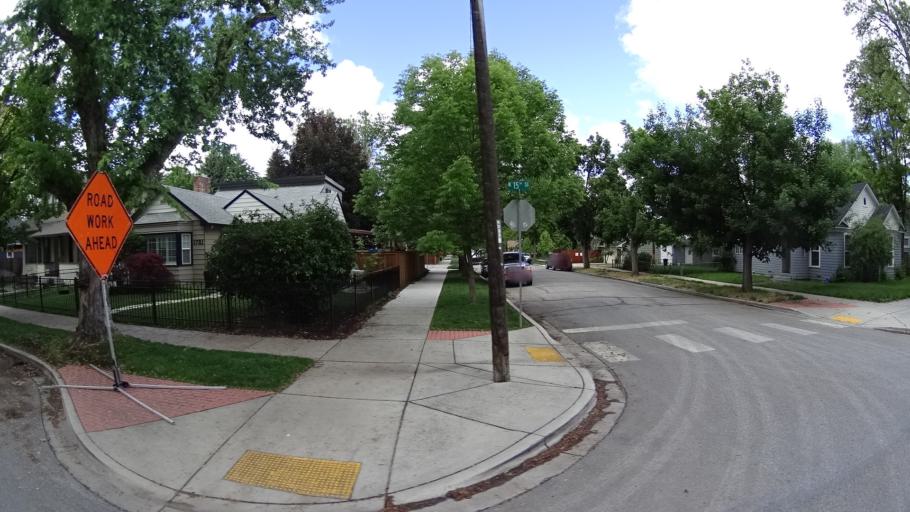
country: US
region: Idaho
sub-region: Ada County
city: Boise
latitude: 43.6338
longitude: -116.2059
